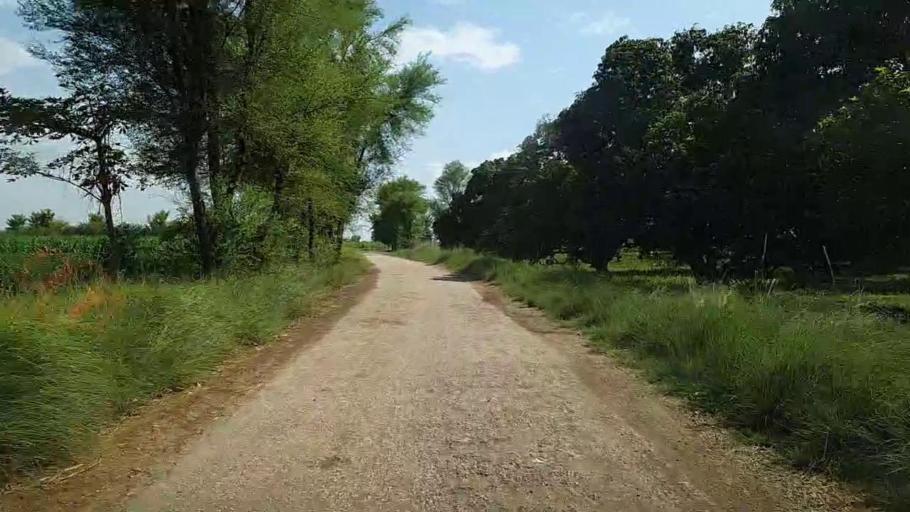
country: PK
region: Sindh
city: Bhiria
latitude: 26.9069
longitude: 68.2251
